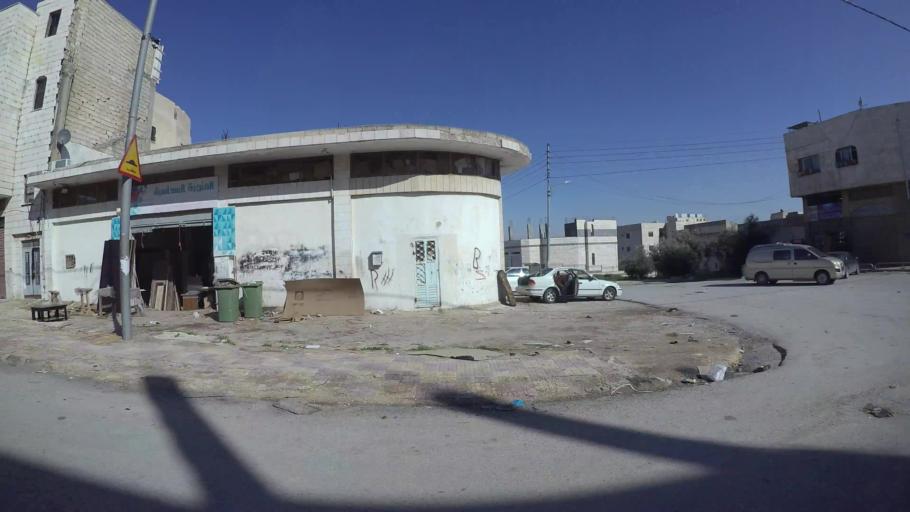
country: JO
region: Amman
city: Al Bunayyat ash Shamaliyah
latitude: 31.9080
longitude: 35.8998
